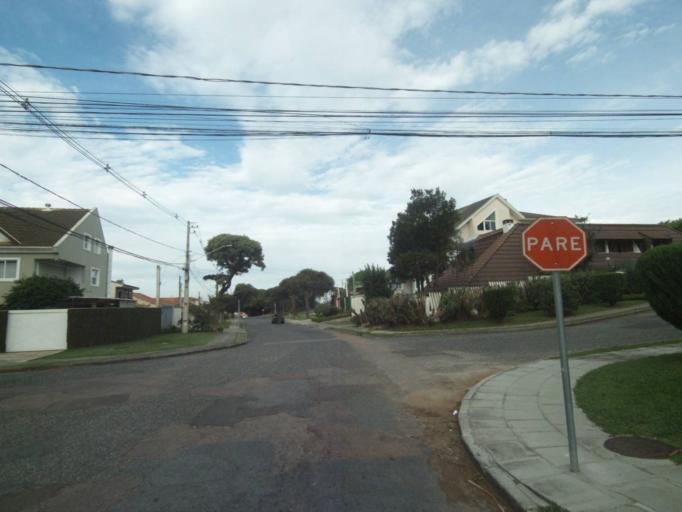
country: BR
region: Parana
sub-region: Curitiba
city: Curitiba
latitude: -25.4313
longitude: -49.2378
